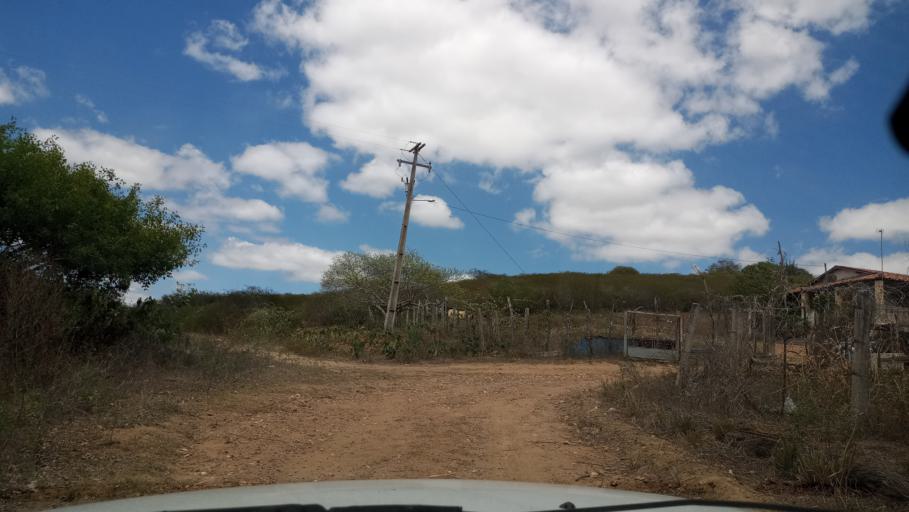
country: BR
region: Rio Grande do Norte
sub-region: Sao Paulo Do Potengi
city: Sao Paulo do Potengi
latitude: -5.7484
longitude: -35.9074
